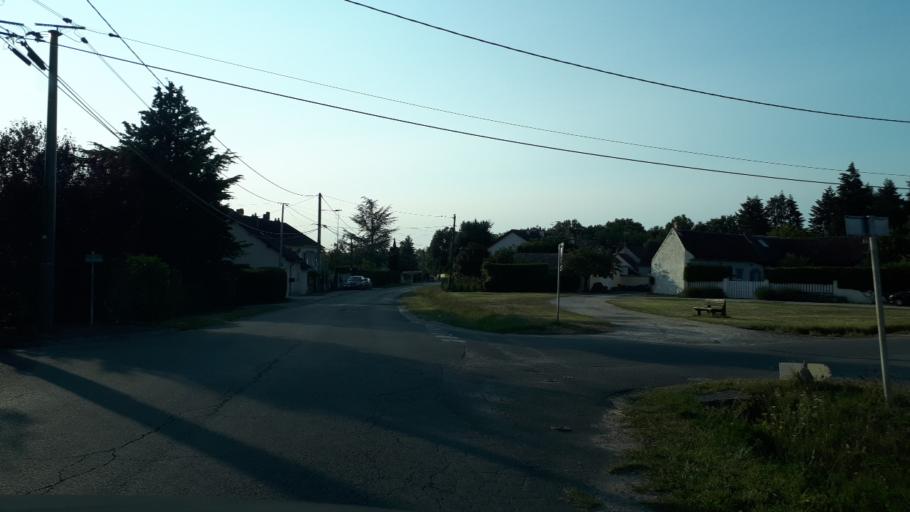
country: FR
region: Centre
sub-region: Departement du Loir-et-Cher
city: Romorantin-Lanthenay
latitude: 47.3433
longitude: 1.7717
